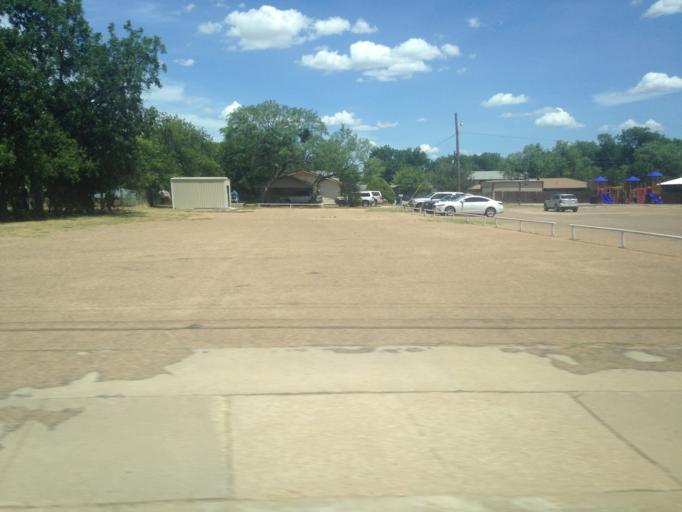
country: US
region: Texas
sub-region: Runnels County
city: Winters
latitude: 31.9631
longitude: -99.9628
